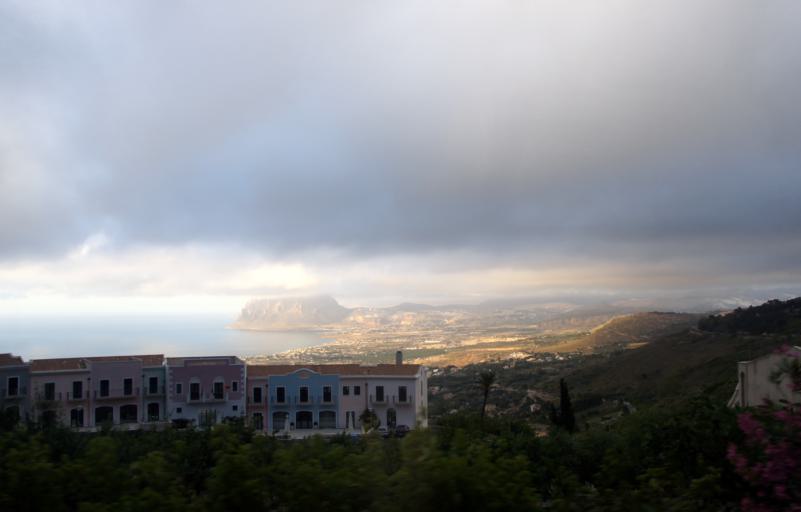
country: IT
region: Sicily
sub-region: Trapani
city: Erice
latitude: 38.0449
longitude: 12.5940
